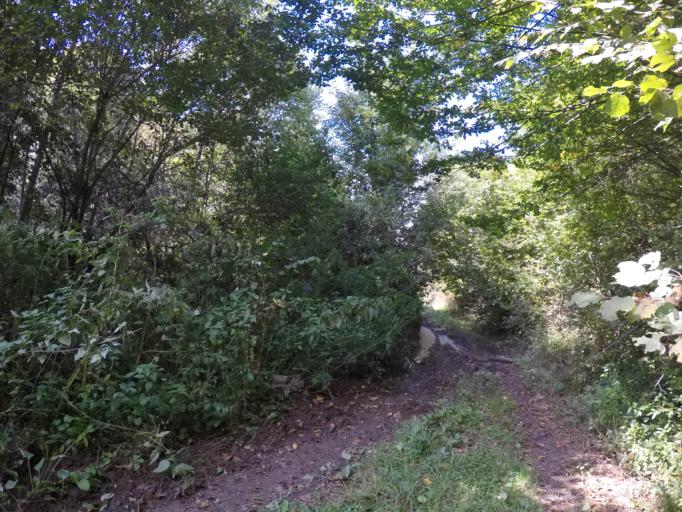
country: SK
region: Presovsky
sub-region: Okres Presov
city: Presov
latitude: 48.9335
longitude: 21.1634
